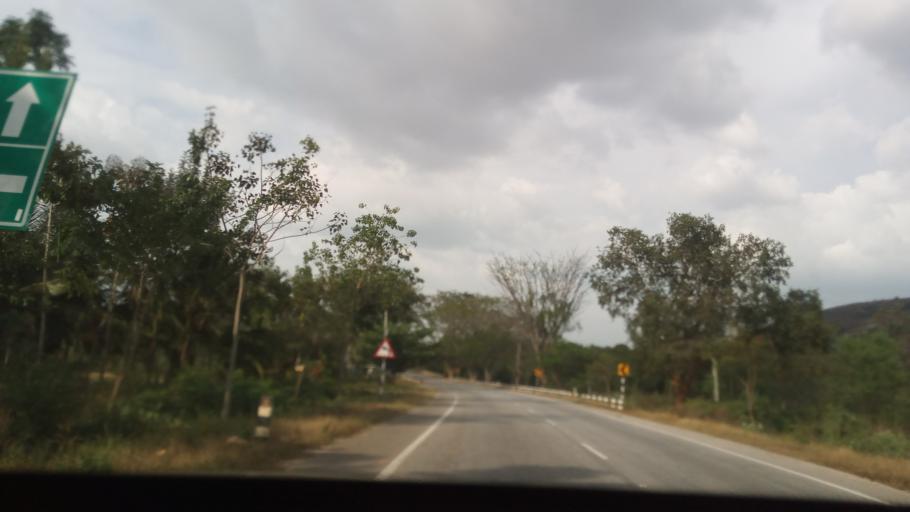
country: IN
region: Karnataka
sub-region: Tumkur
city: Kunigal
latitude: 12.8039
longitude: 77.0382
